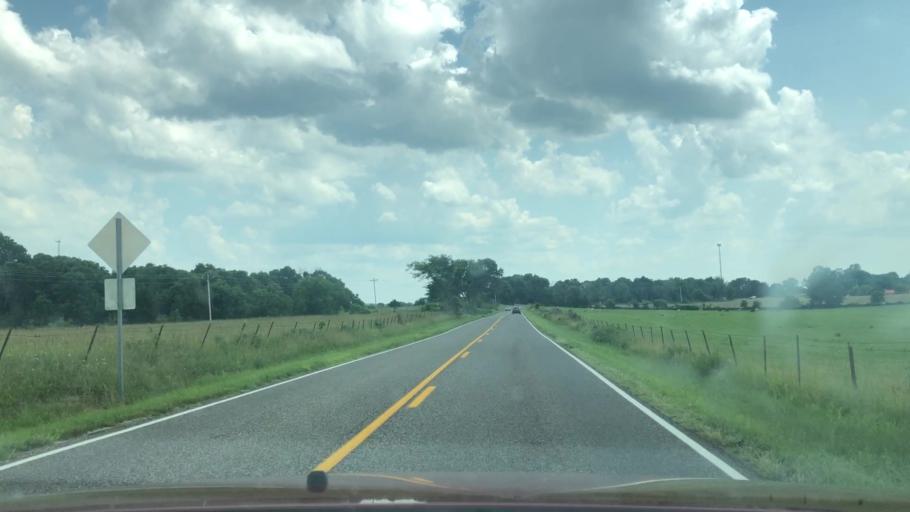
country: US
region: Missouri
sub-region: Christian County
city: Ozark
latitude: 36.9397
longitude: -93.2536
